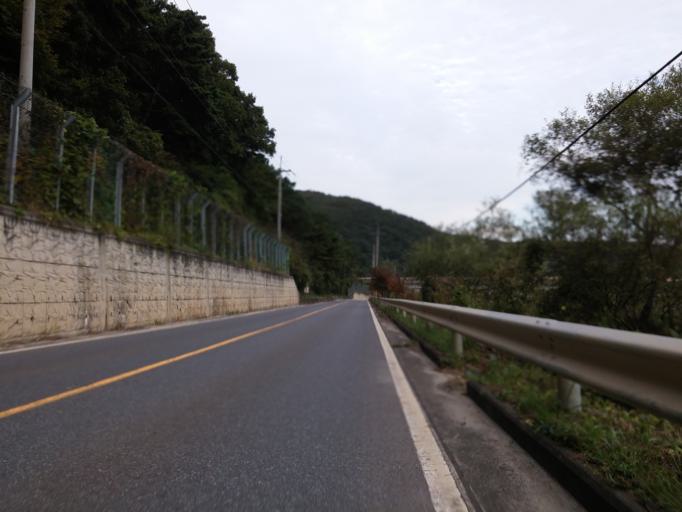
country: KR
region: Daejeon
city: Daejeon
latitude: 36.2205
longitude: 127.2742
